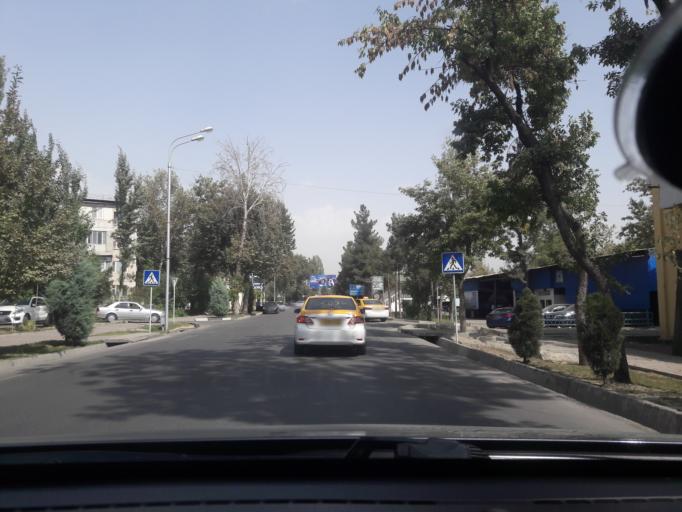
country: TJ
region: Dushanbe
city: Dushanbe
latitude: 38.5666
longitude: 68.7642
